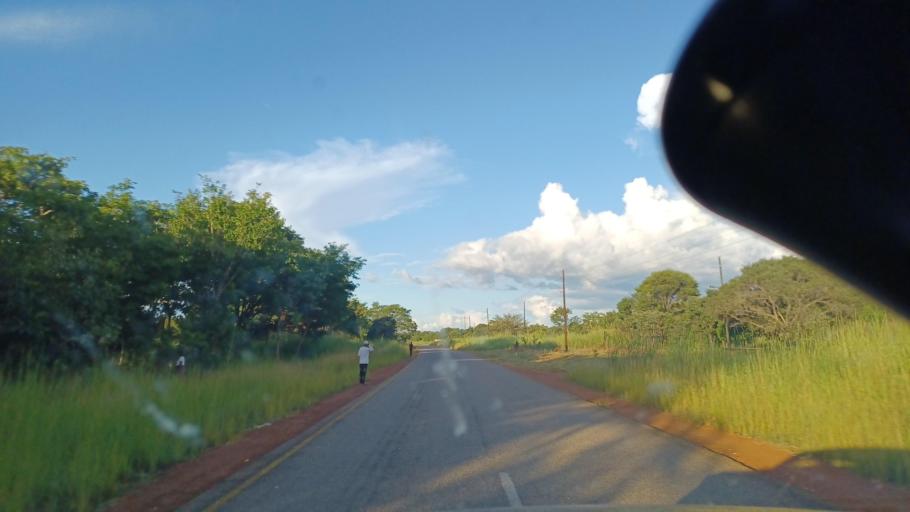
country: ZM
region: North-Western
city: Kalengwa
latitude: -13.1340
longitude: 25.1660
